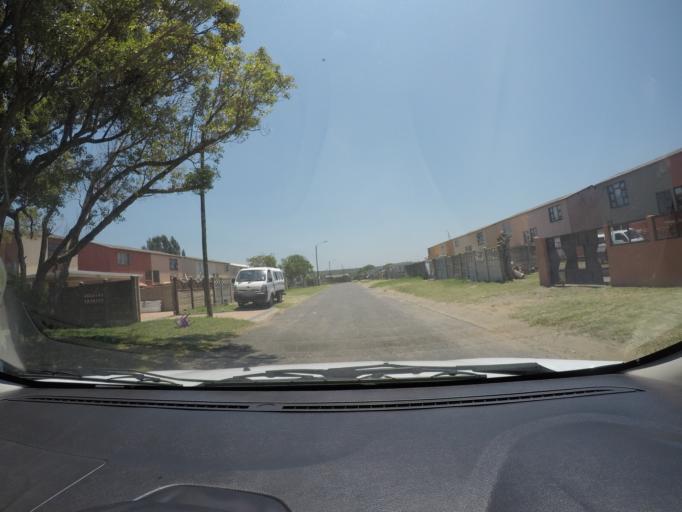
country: ZA
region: KwaZulu-Natal
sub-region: uThungulu District Municipality
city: eSikhawini
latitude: -28.8735
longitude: 31.9040
